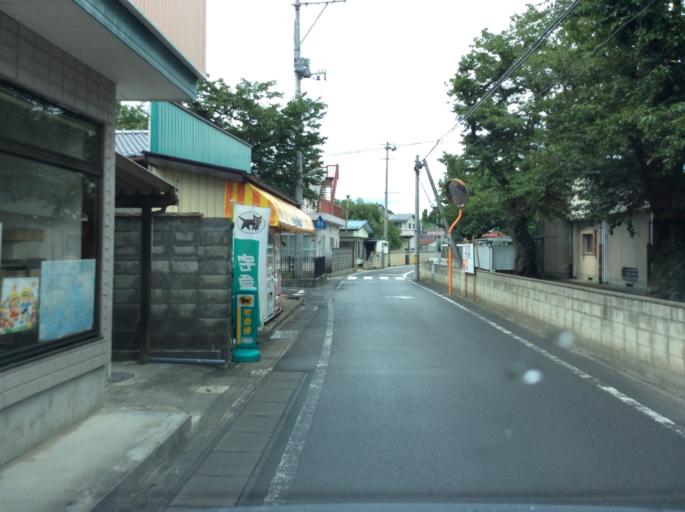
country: JP
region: Fukushima
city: Fukushima-shi
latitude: 37.7954
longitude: 140.4232
